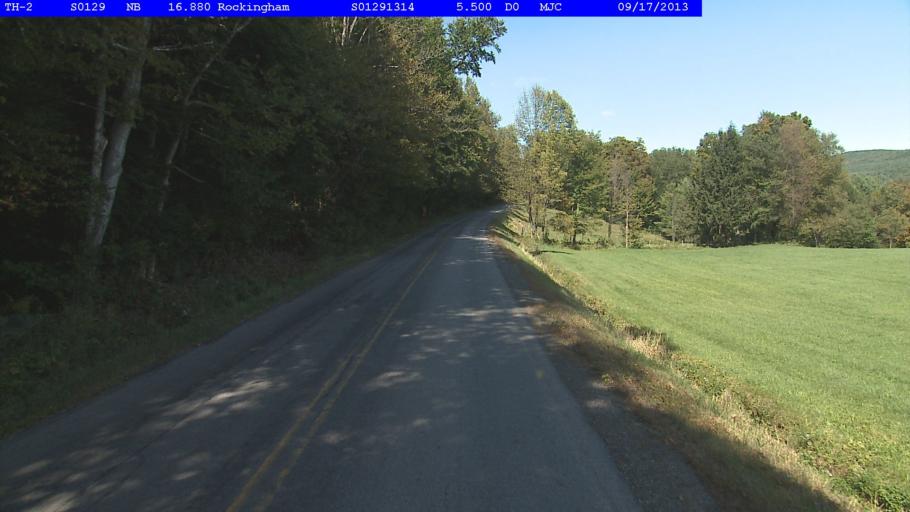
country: US
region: Vermont
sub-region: Windham County
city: Rockingham
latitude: 43.1956
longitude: -72.5117
